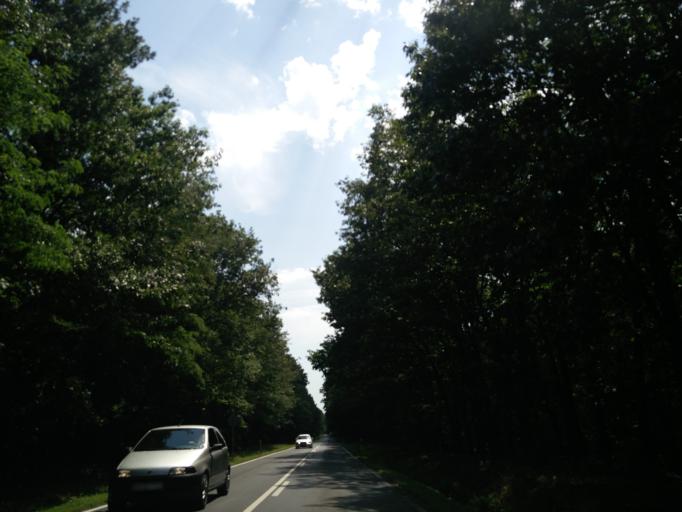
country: HU
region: Zala
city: Zalaegerszeg
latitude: 46.8935
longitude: 16.8554
